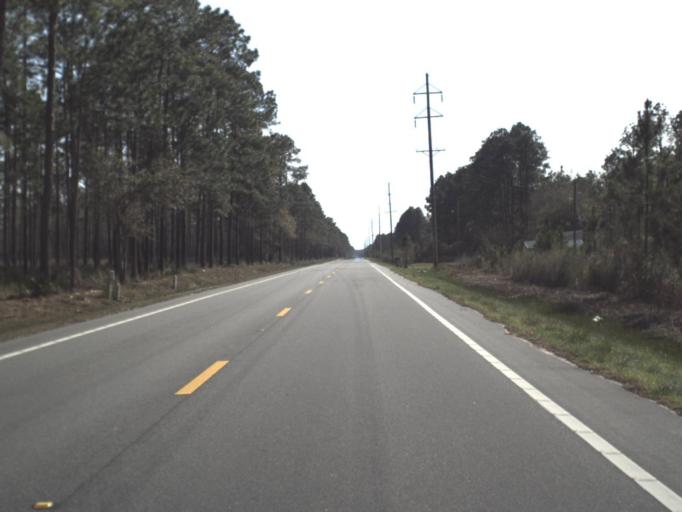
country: US
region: Florida
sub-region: Wakulla County
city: Crawfordville
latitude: 30.0378
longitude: -84.4963
